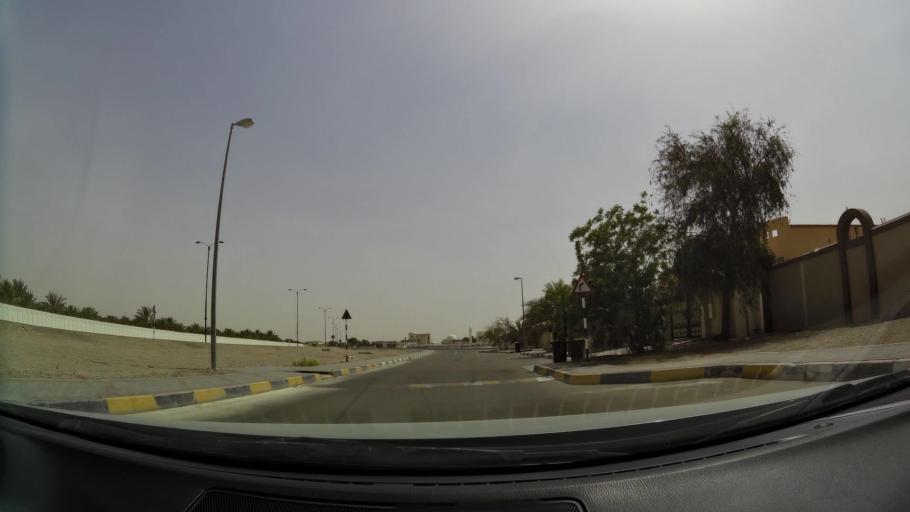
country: AE
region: Abu Dhabi
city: Al Ain
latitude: 24.1476
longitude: 55.6522
